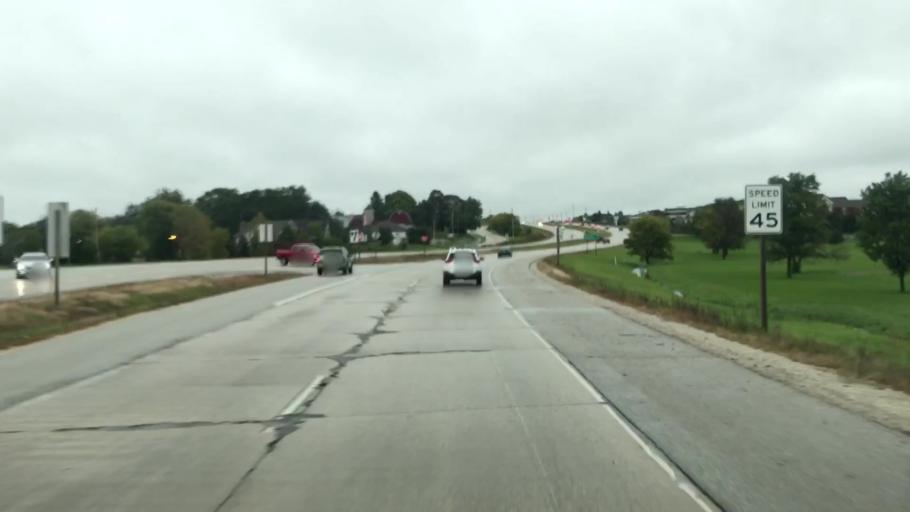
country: US
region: Wisconsin
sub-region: Waukesha County
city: Pewaukee
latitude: 43.0835
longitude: -88.2494
